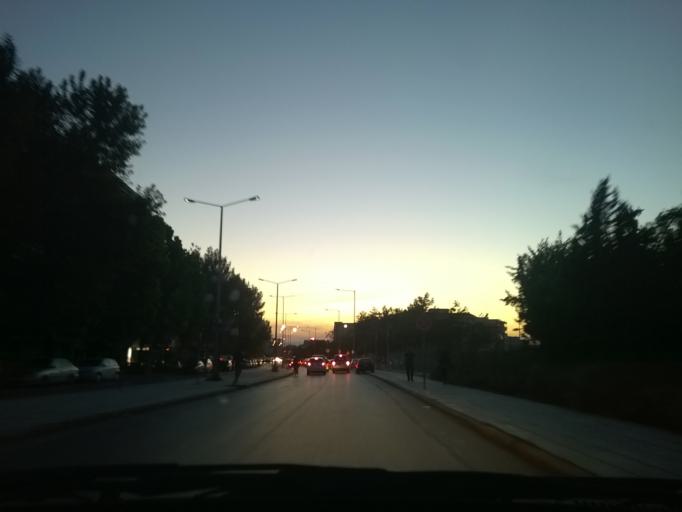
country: GR
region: Central Macedonia
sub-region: Nomos Thessalonikis
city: Ampelokipoi
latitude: 40.6570
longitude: 22.9362
